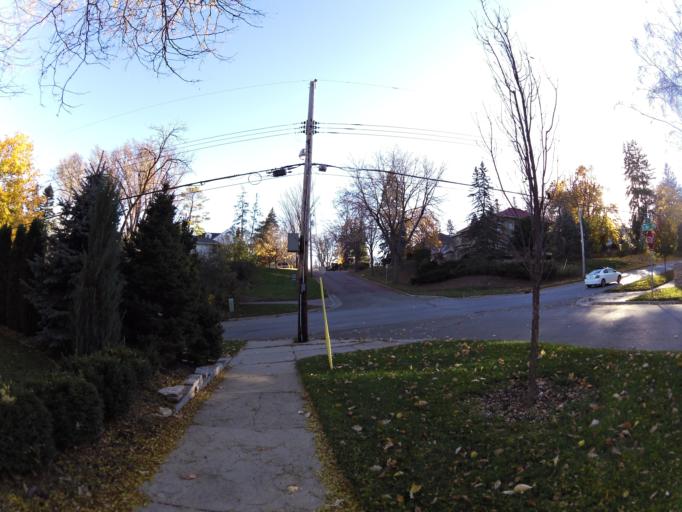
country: US
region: Minnesota
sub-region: Olmsted County
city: Rochester
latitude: 44.0173
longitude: -92.4762
